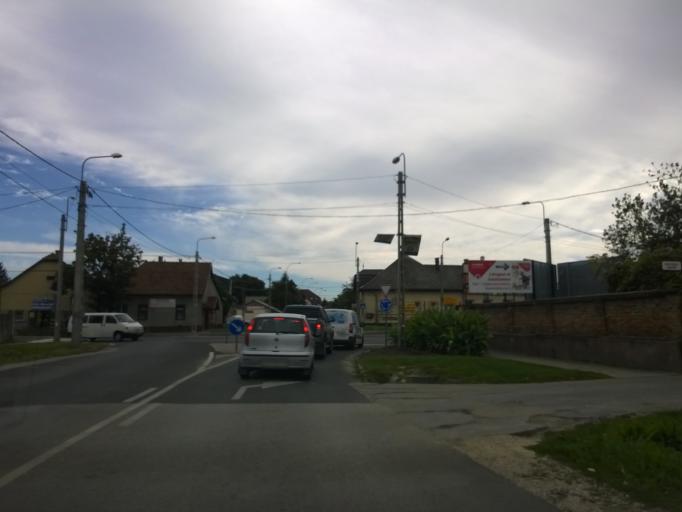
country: HU
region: Pest
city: Szigetszentmiklos
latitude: 47.3498
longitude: 19.0431
